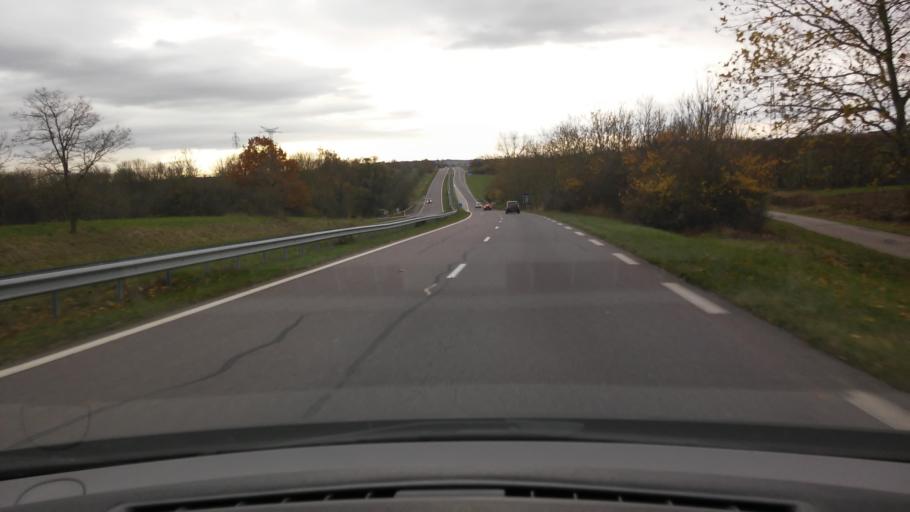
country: FR
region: Lorraine
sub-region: Departement de la Moselle
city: Argancy
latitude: 49.2061
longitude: 6.2088
